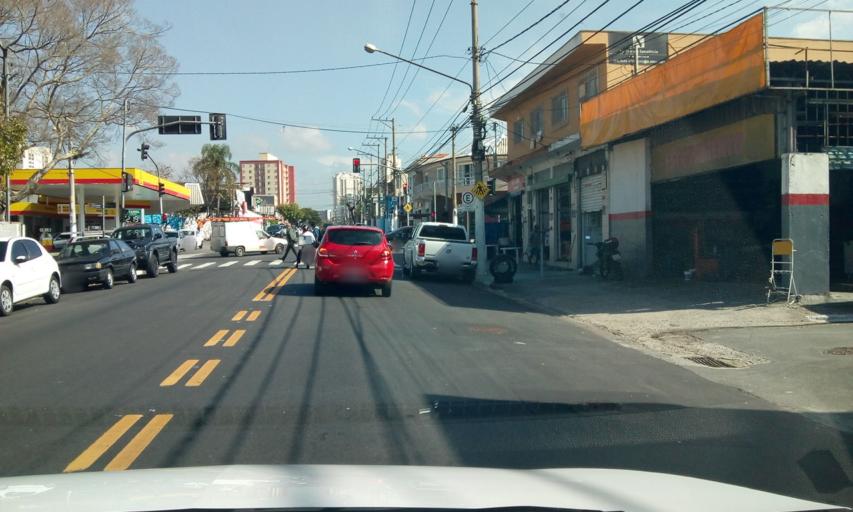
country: BR
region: Sao Paulo
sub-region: Osasco
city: Osasco
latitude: -23.5493
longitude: -46.7775
